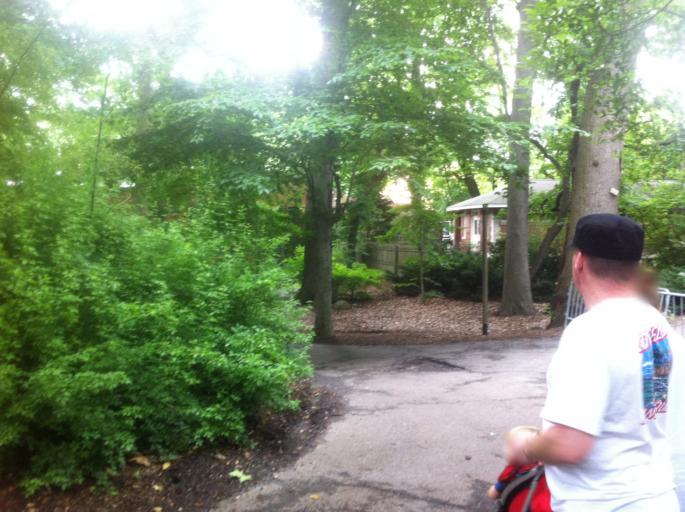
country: US
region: New York
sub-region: Bronx
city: The Bronx
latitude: 40.8510
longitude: -73.8793
